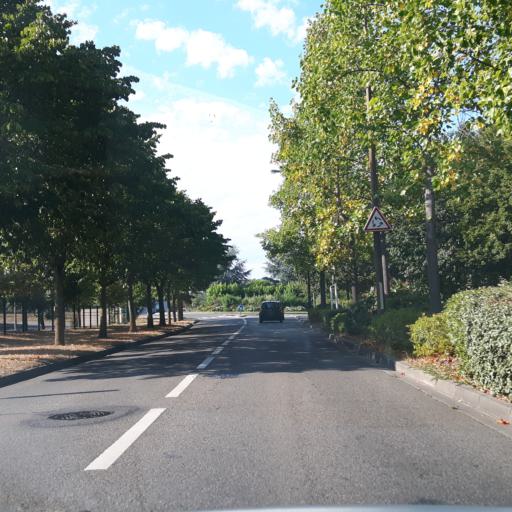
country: FR
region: Midi-Pyrenees
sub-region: Departement de la Haute-Garonne
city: Balma
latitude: 43.5894
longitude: 1.4910
